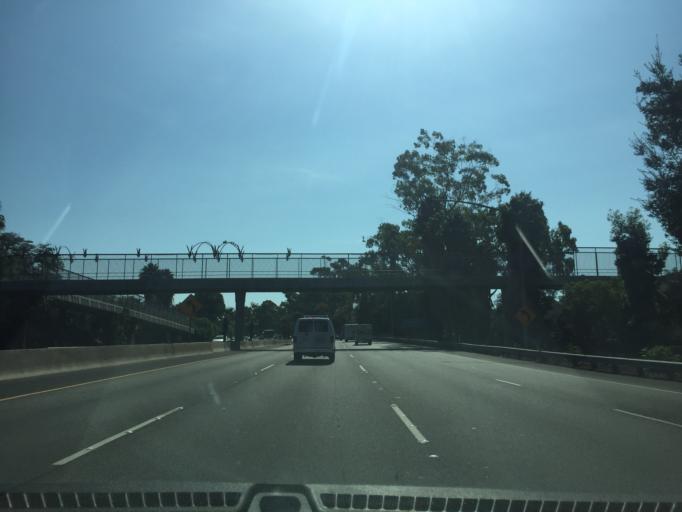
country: US
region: California
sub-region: Santa Barbara County
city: Santa Barbara
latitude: 34.4148
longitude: -119.7054
